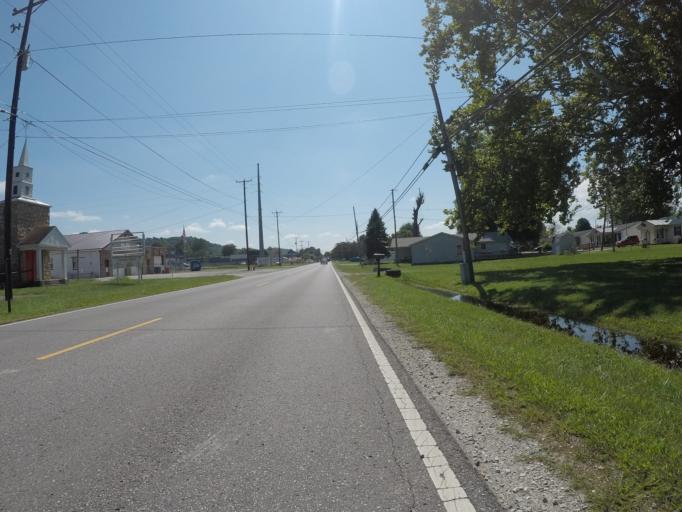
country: US
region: Kentucky
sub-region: Boyd County
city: Ashland
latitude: 38.4643
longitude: -82.6015
